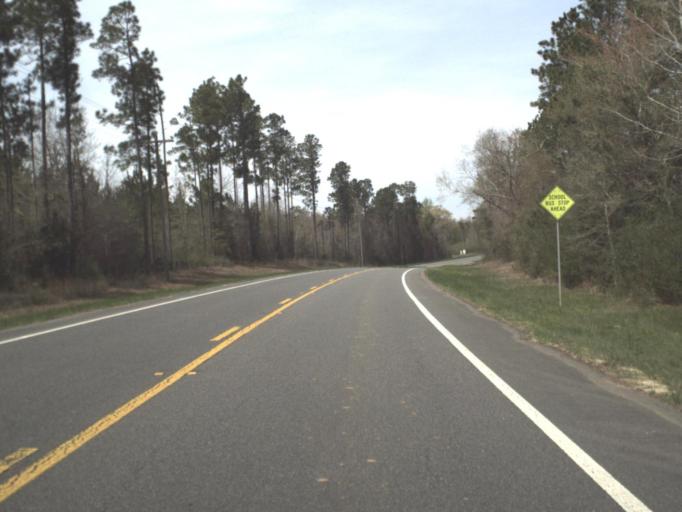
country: US
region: Alabama
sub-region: Geneva County
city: Geneva
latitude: 30.9616
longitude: -85.9949
